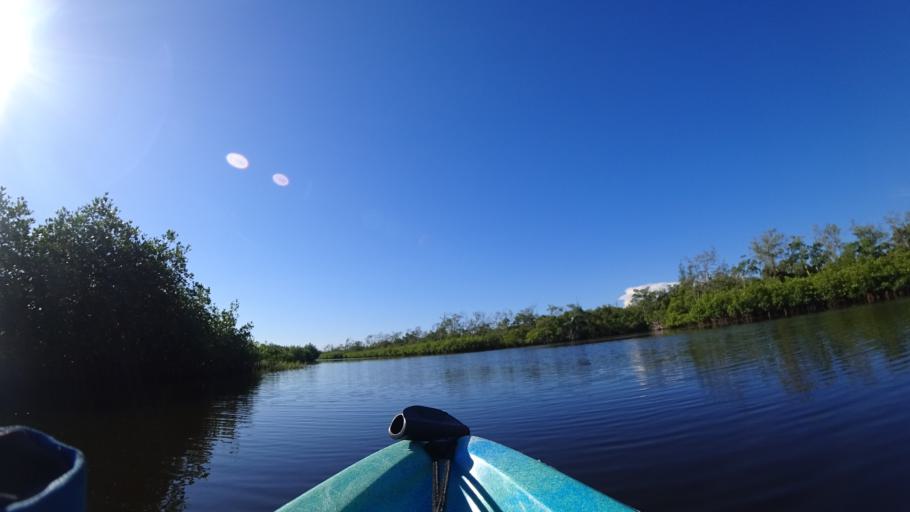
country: US
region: Florida
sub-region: Manatee County
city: Cortez
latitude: 27.5005
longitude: -82.6648
